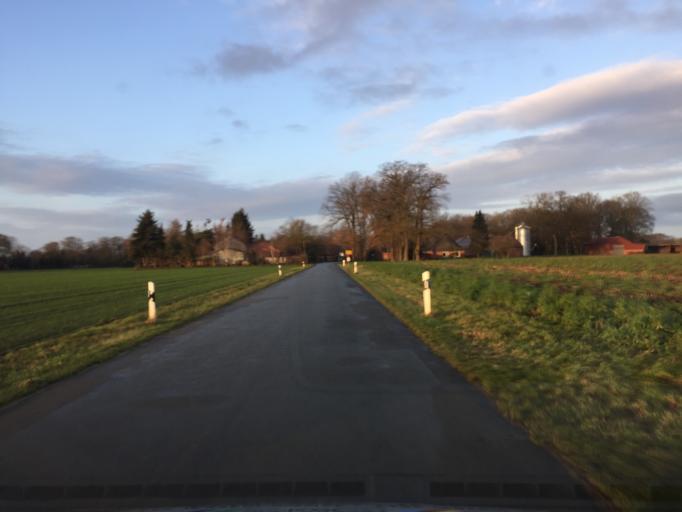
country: DE
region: Lower Saxony
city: Raddestorf
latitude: 52.4221
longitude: 8.9256
